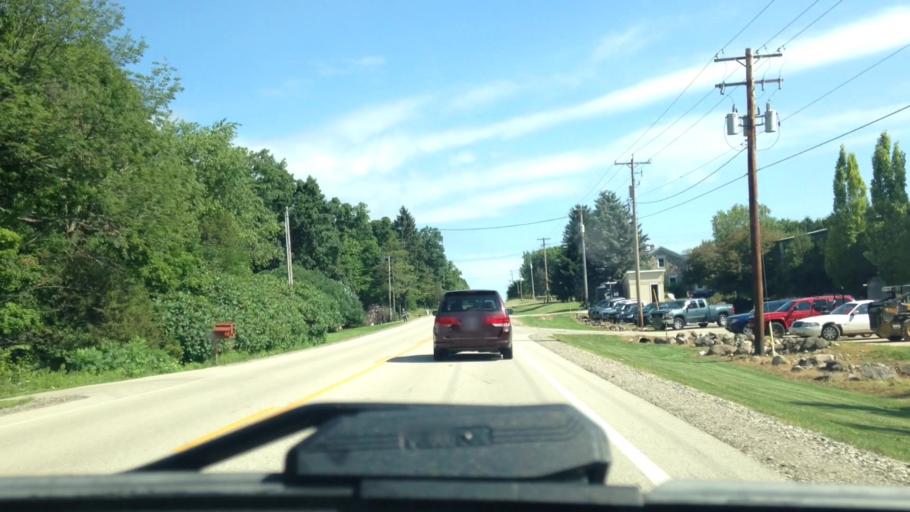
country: US
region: Wisconsin
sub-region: Washington County
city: West Bend
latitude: 43.4025
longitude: -88.2410
